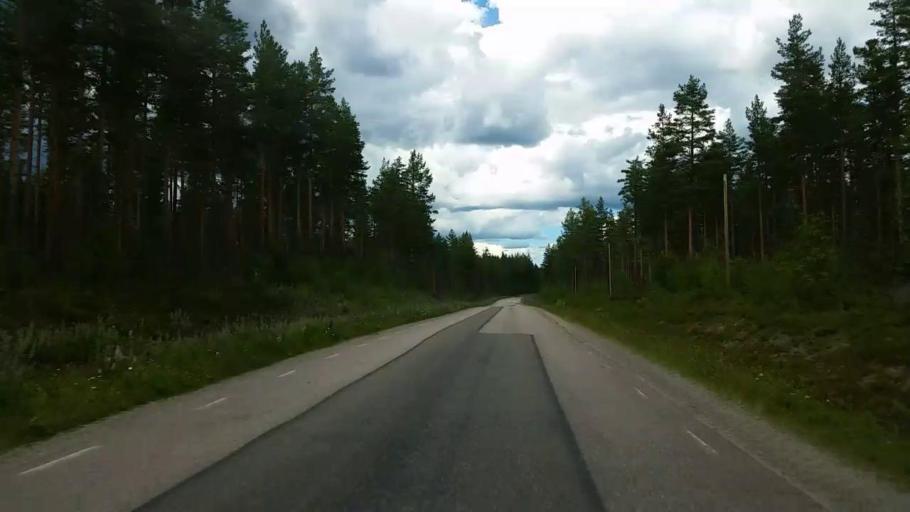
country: SE
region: Gaevleborg
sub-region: Ovanakers Kommun
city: Edsbyn
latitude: 61.4068
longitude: 15.8967
